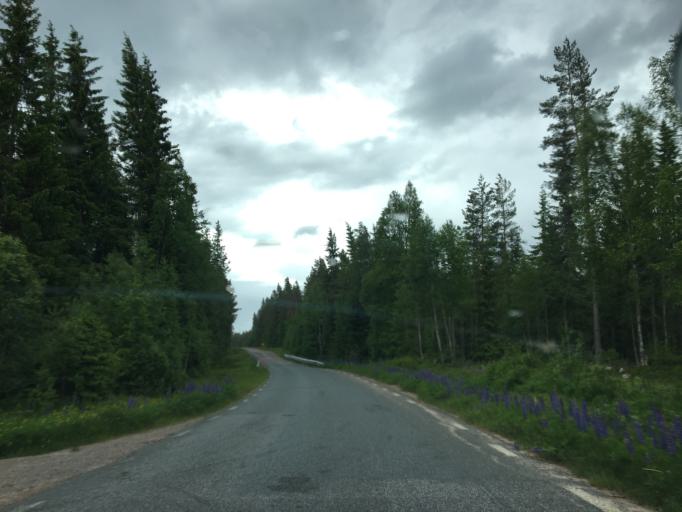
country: SE
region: Vaermland
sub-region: Filipstads Kommun
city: Lesjofors
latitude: 60.1150
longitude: 14.4649
